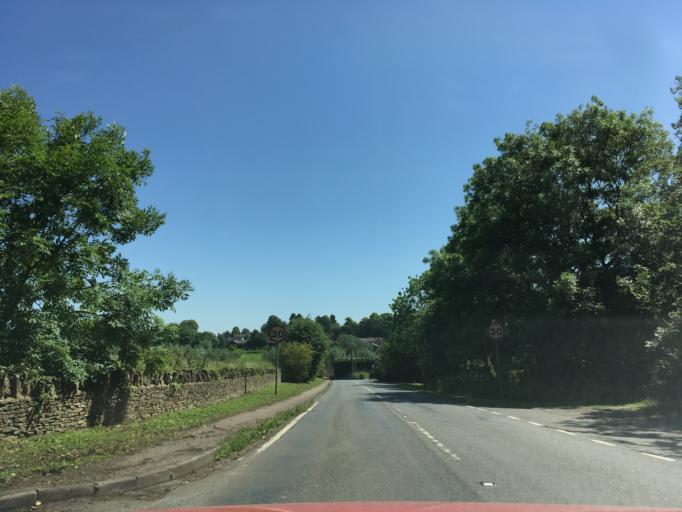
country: GB
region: England
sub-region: Oxfordshire
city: Somerton
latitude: 51.9963
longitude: -1.2195
